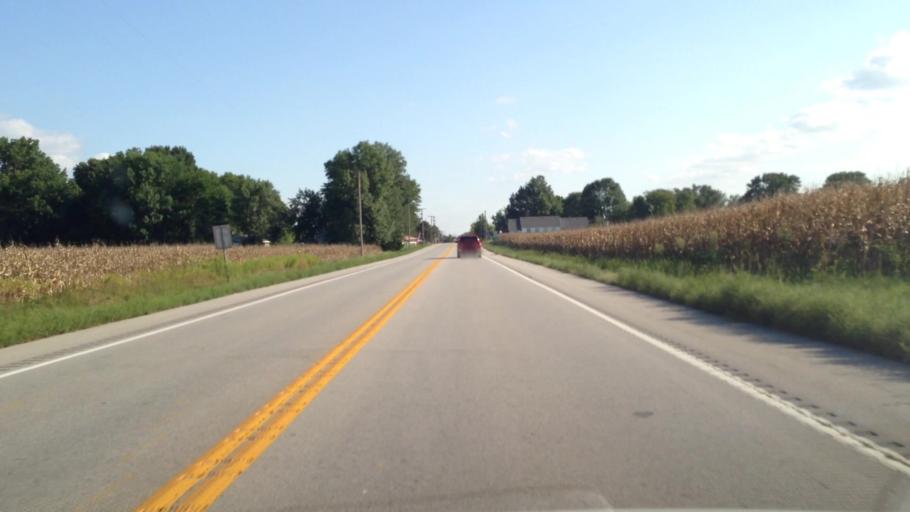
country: US
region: Missouri
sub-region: Jasper County
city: Carl Junction
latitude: 37.2785
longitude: -94.6010
